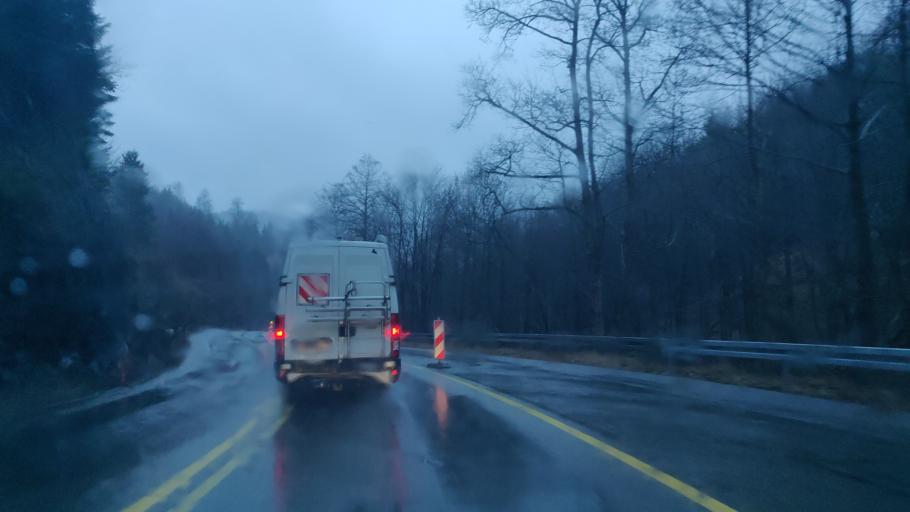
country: DE
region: Lower Saxony
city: Braunlage
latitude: 51.7022
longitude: 10.5728
